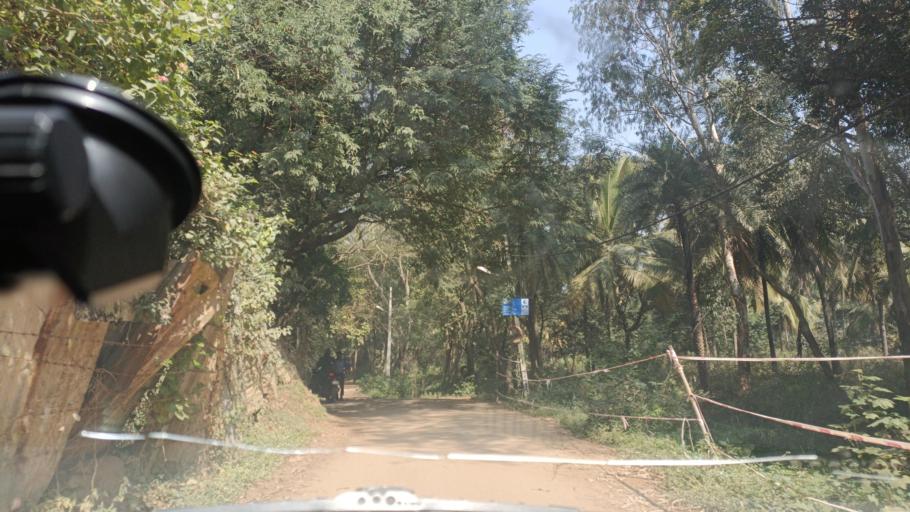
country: IN
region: Karnataka
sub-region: Bangalore Urban
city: Yelahanka
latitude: 13.1177
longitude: 77.6007
